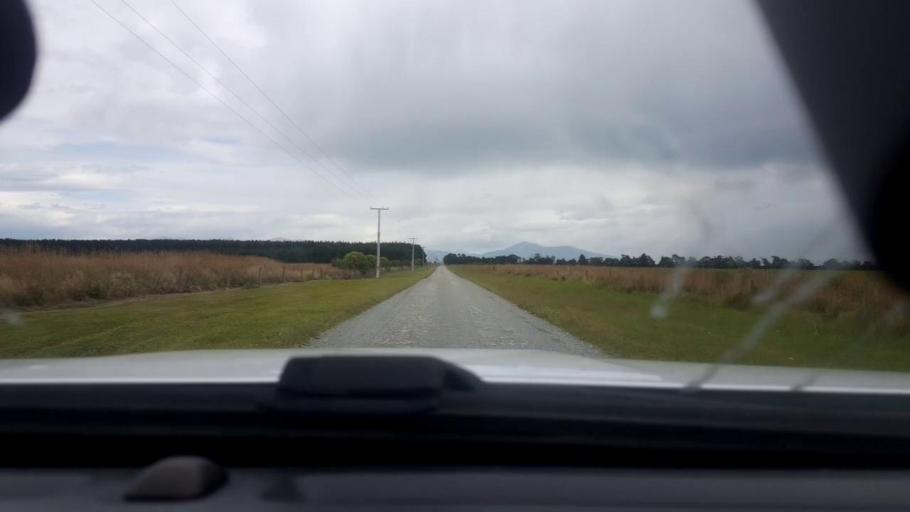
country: NZ
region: Canterbury
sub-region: Timaru District
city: Timaru
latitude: -44.1649
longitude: 171.4090
